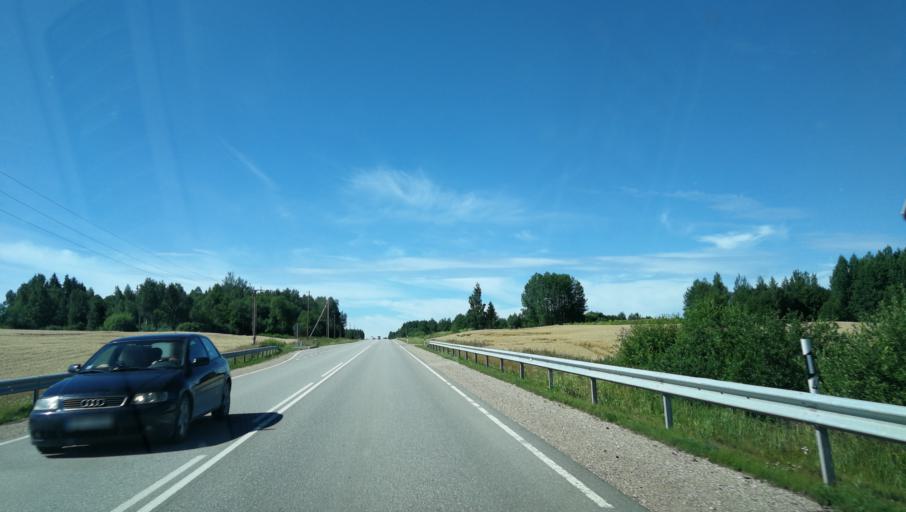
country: LV
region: Gulbenes Rajons
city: Gulbene
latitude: 57.1102
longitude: 26.6611
